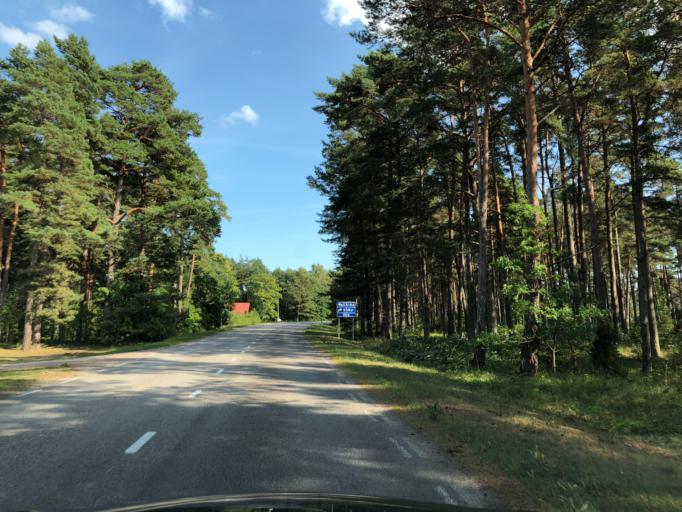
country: EE
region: Hiiumaa
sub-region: Kaerdla linn
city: Kardla
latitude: 58.7073
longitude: 22.5924
